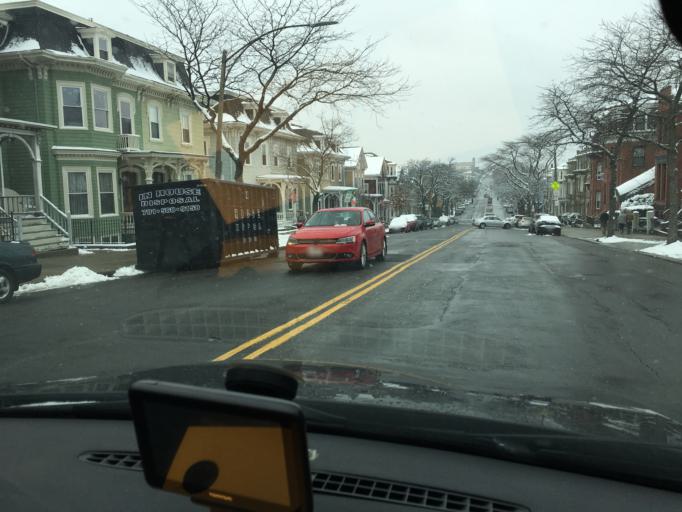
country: US
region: Massachusetts
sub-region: Suffolk County
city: South Boston
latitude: 42.3357
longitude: -71.0334
